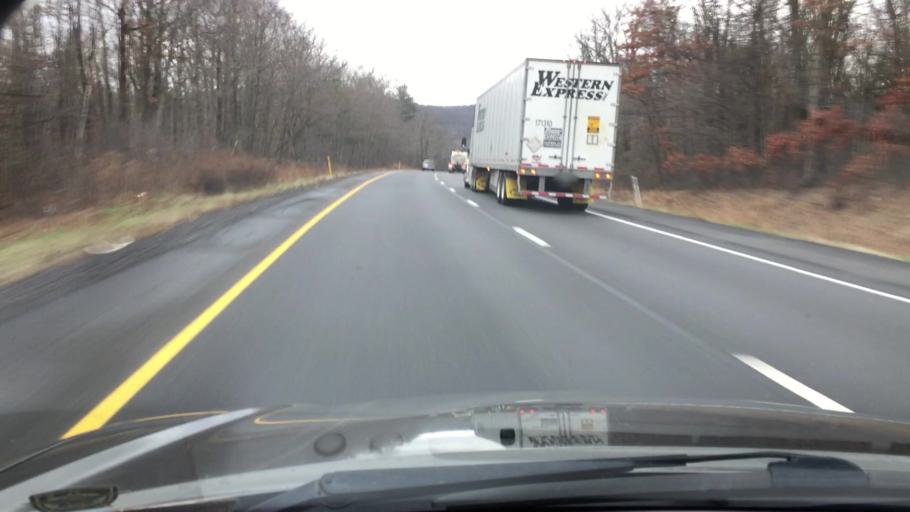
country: US
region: Pennsylvania
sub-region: Luzerne County
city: Freeland
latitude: 41.0565
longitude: -75.8577
